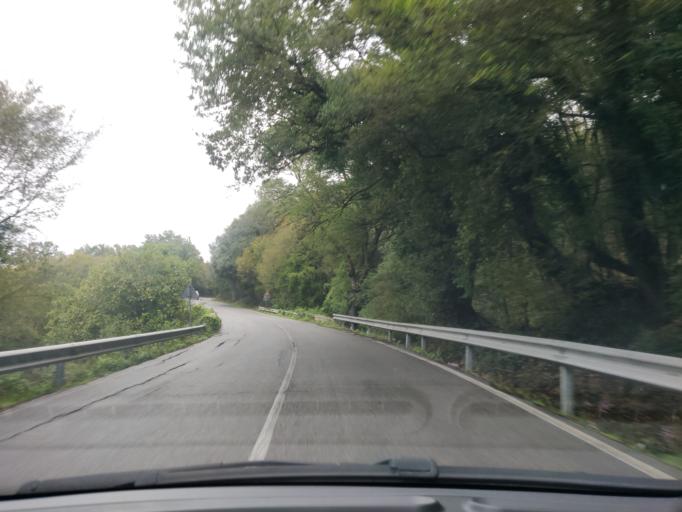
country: IT
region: Latium
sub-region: Citta metropolitana di Roma Capitale
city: Allumiere
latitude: 42.1392
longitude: 11.8730
